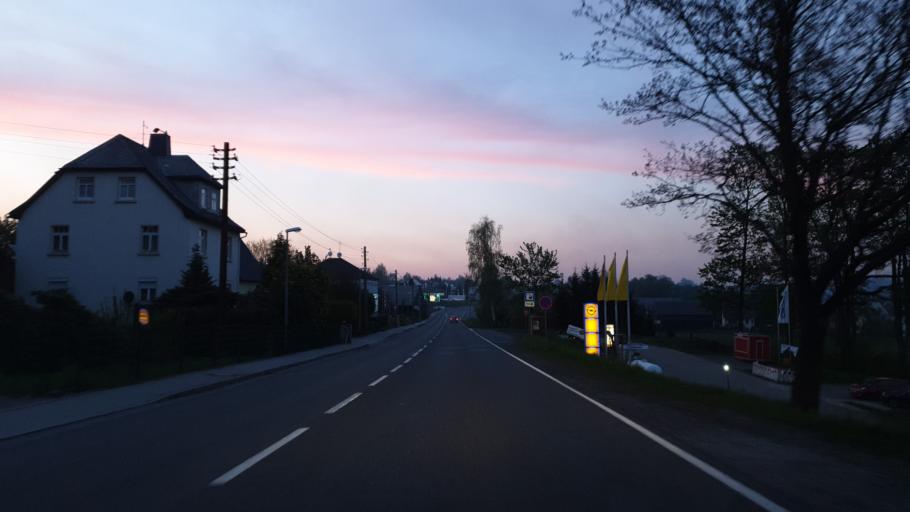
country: DE
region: Saxony
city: Stollberg
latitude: 50.7192
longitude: 12.7850
